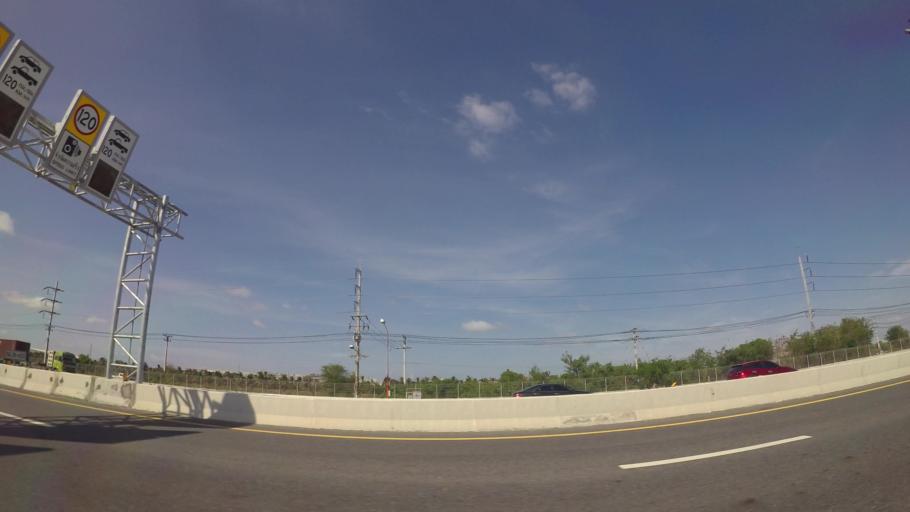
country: TH
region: Bangkok
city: Lat Krabang
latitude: 13.7124
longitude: 100.7663
